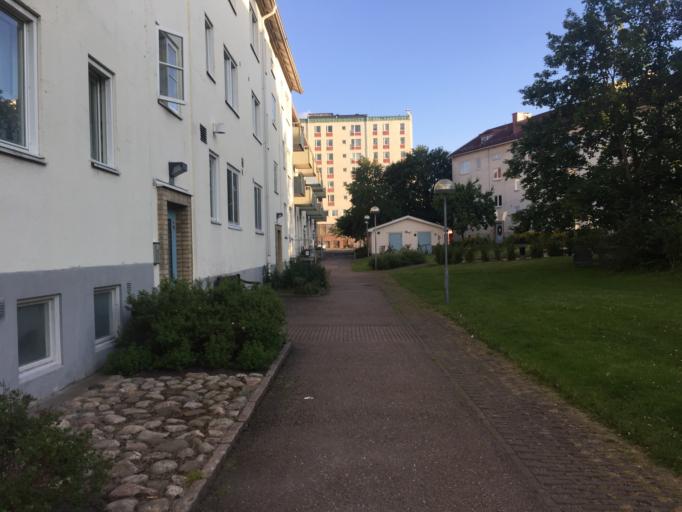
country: SE
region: Vaestra Goetaland
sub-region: Goteborg
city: Goeteborg
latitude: 57.7228
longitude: 11.9368
